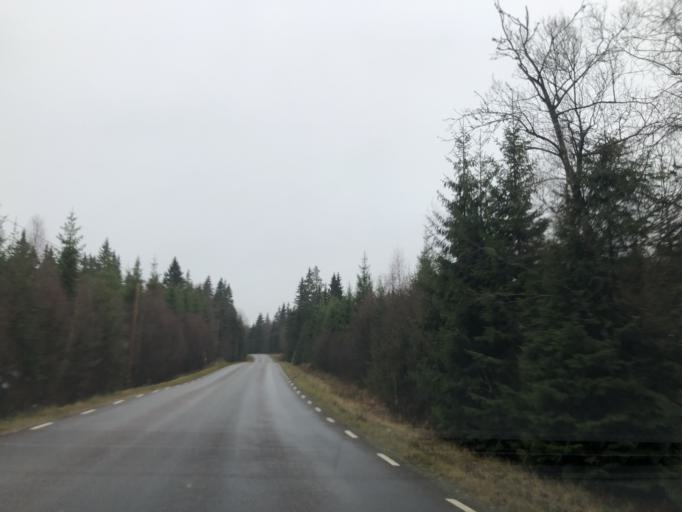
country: SE
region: Vaestra Goetaland
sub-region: Ulricehamns Kommun
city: Ulricehamn
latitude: 57.7525
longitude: 13.5167
